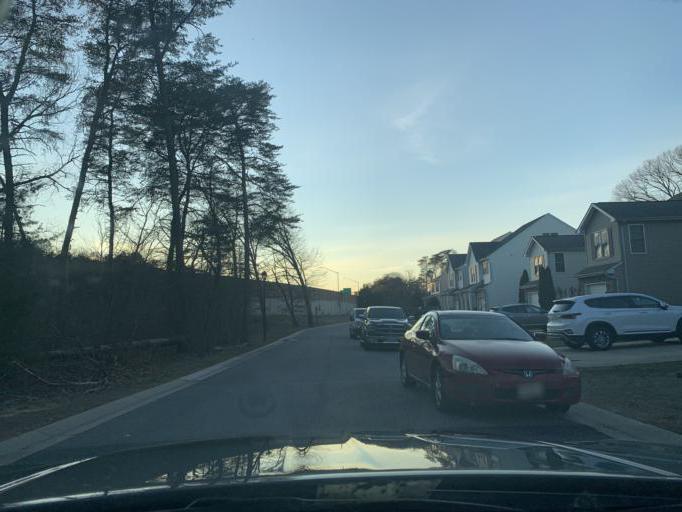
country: US
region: Maryland
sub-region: Anne Arundel County
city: Glen Burnie
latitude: 39.1536
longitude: -76.6378
